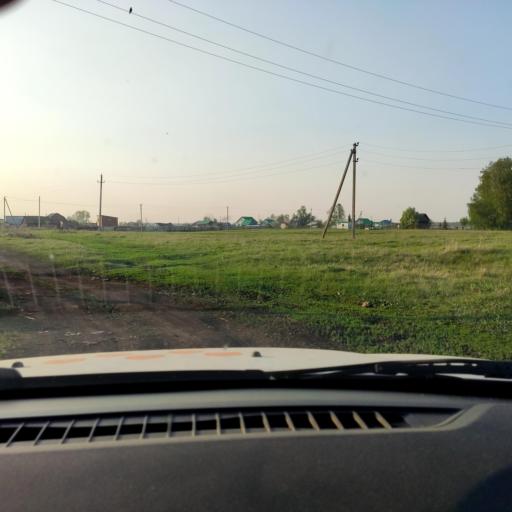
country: RU
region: Bashkortostan
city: Mikhaylovka
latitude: 54.9573
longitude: 55.8036
